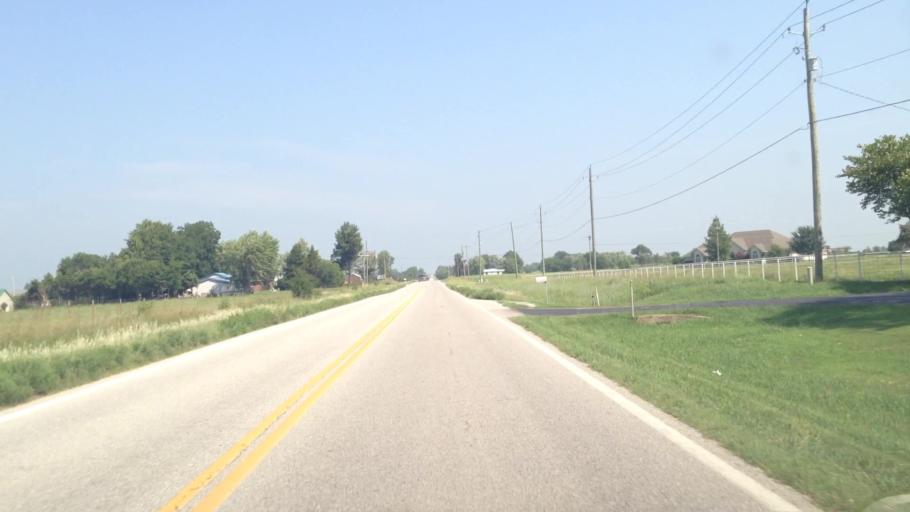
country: US
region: Oklahoma
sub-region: Craig County
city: Vinita
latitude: 36.6686
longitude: -95.1436
